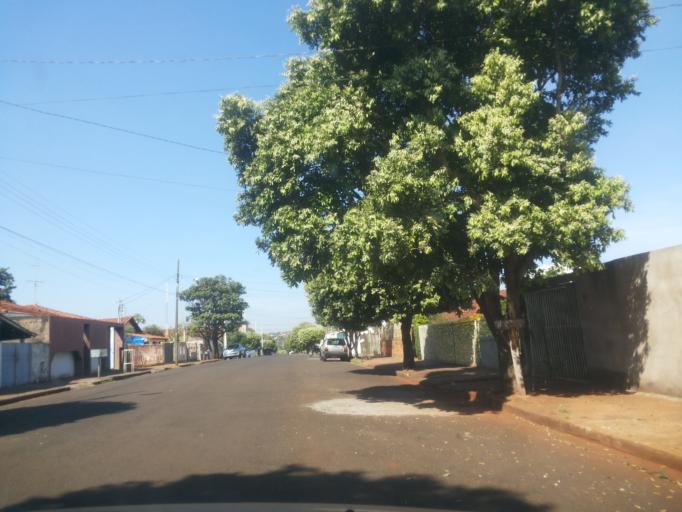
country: BR
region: Minas Gerais
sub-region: Ituiutaba
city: Ituiutaba
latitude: -18.9677
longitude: -49.4531
